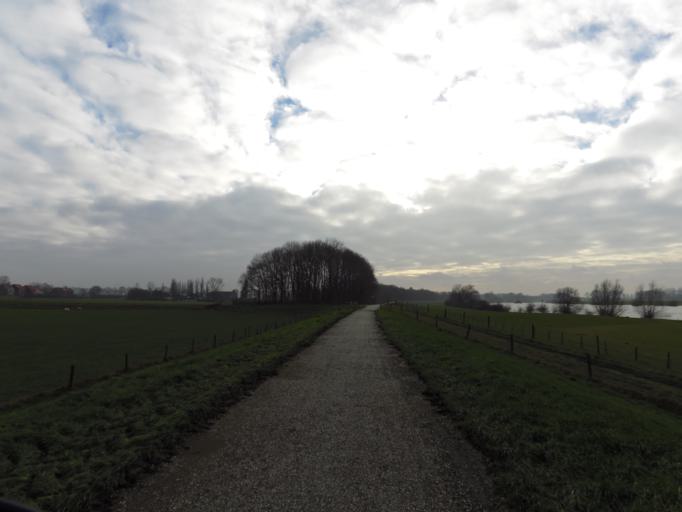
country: NL
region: Gelderland
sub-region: Gemeente Doesburg
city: Doesburg
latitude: 52.0016
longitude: 6.1152
